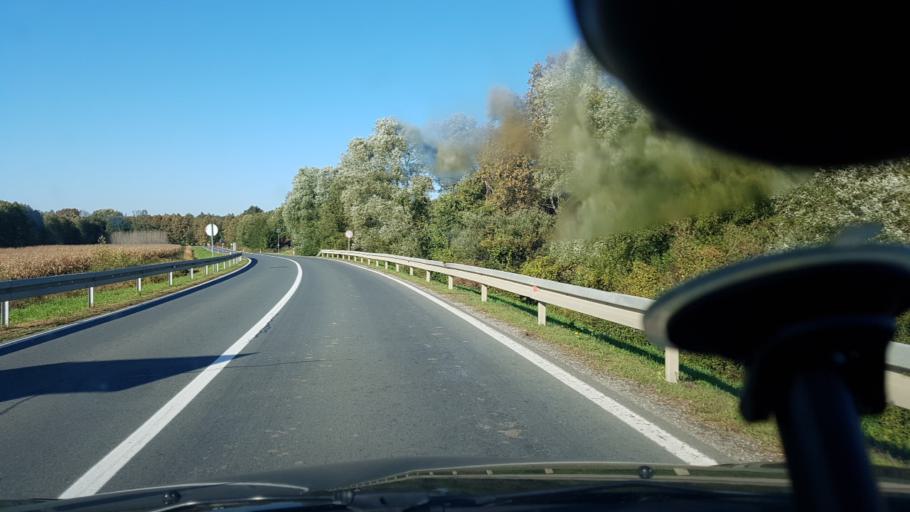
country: HR
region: Bjelovarsko-Bilogorska
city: Brezovac
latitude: 45.8393
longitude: 16.8223
